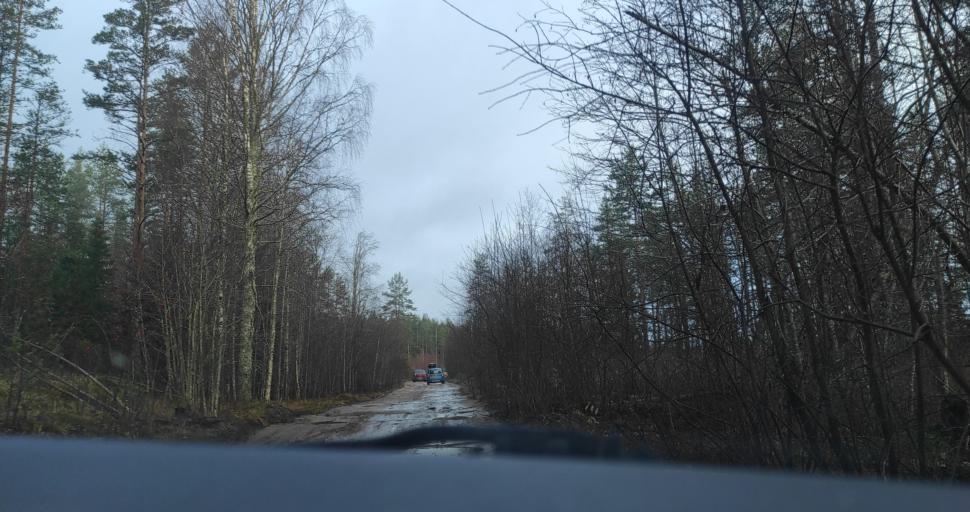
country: RU
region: Republic of Karelia
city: Pitkyaranta
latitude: 61.7397
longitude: 31.3911
